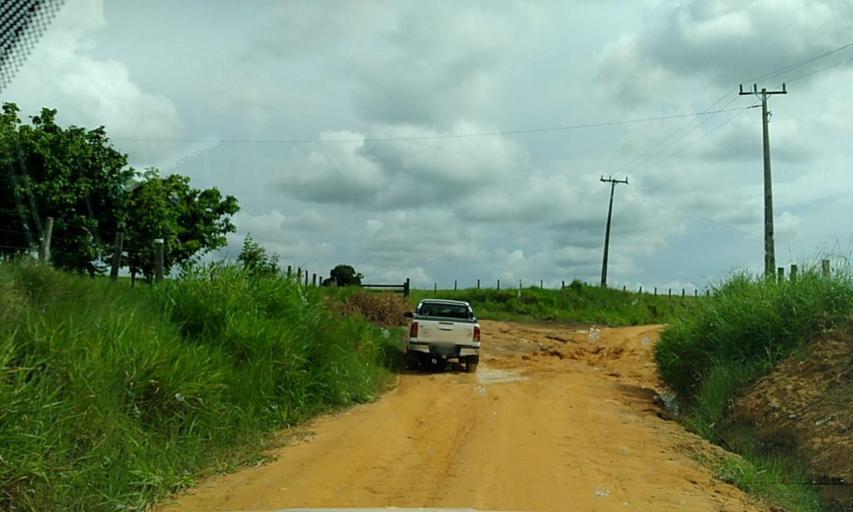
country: BR
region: Para
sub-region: Altamira
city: Altamira
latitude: -3.2533
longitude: -52.6939
